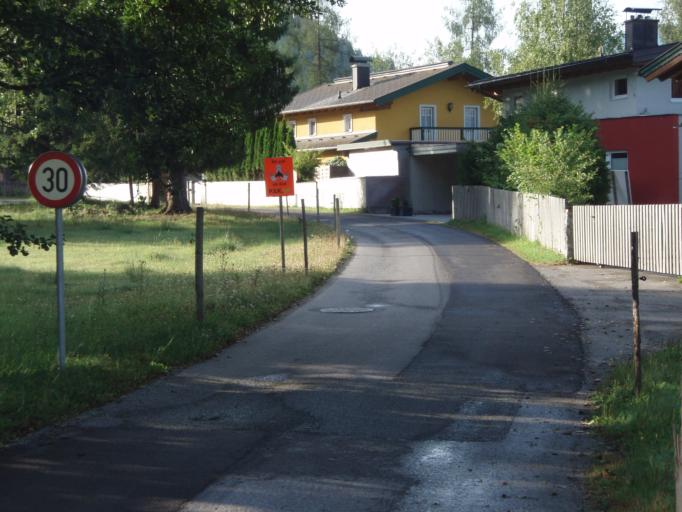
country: AT
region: Salzburg
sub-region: Politischer Bezirk Sankt Johann im Pongau
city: Werfenweng
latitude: 47.4627
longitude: 13.2454
